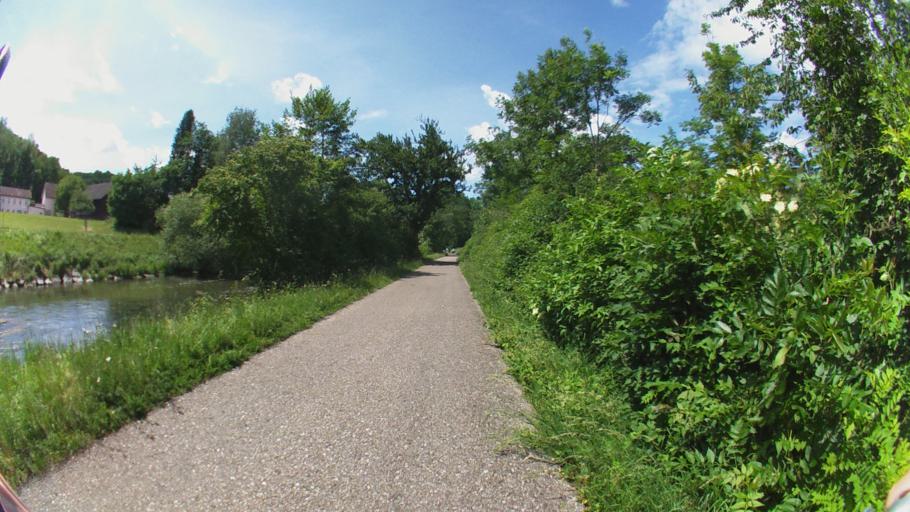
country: CH
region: Zurich
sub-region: Bezirk Buelach
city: Glattfelden
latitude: 47.5492
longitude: 8.5222
